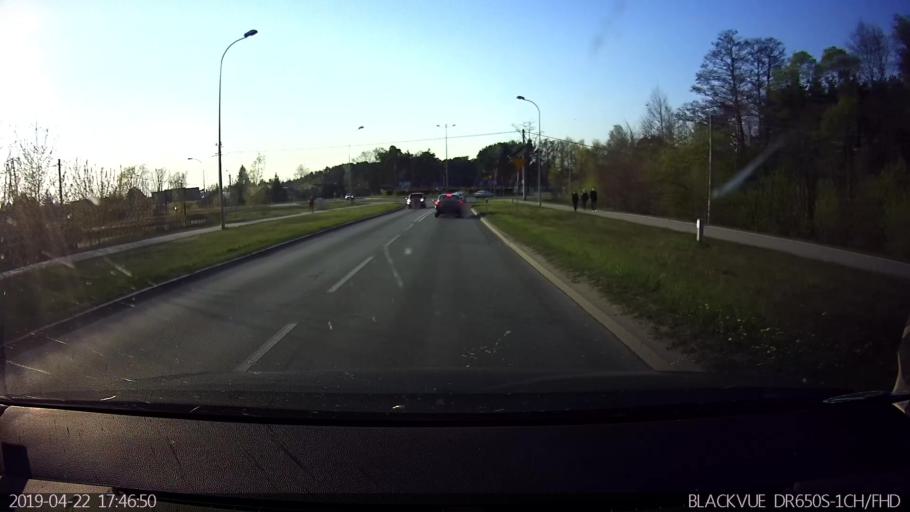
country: PL
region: Masovian Voivodeship
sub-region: Powiat wegrowski
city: Wegrow
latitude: 52.4035
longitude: 22.0238
